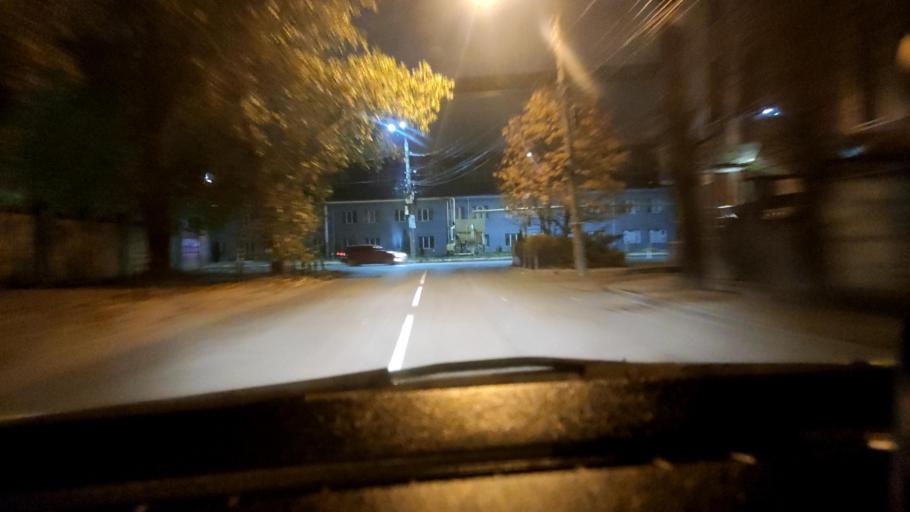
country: RU
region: Voronezj
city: Voronezh
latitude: 51.6867
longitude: 39.1698
